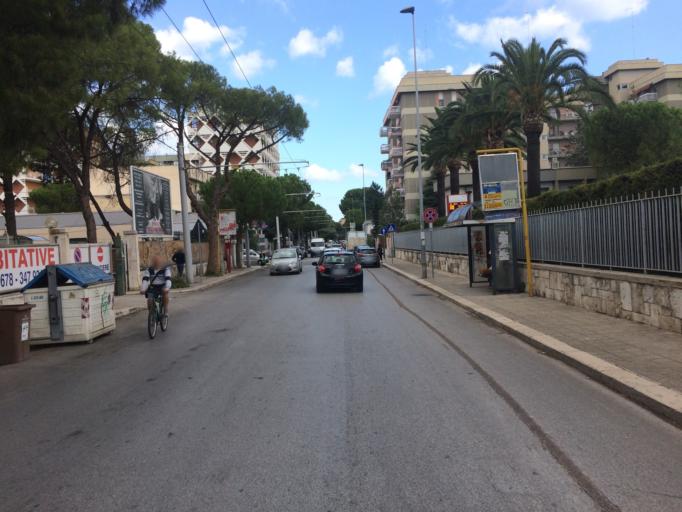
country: IT
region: Apulia
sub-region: Provincia di Bari
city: Bari
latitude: 41.0962
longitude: 16.8709
